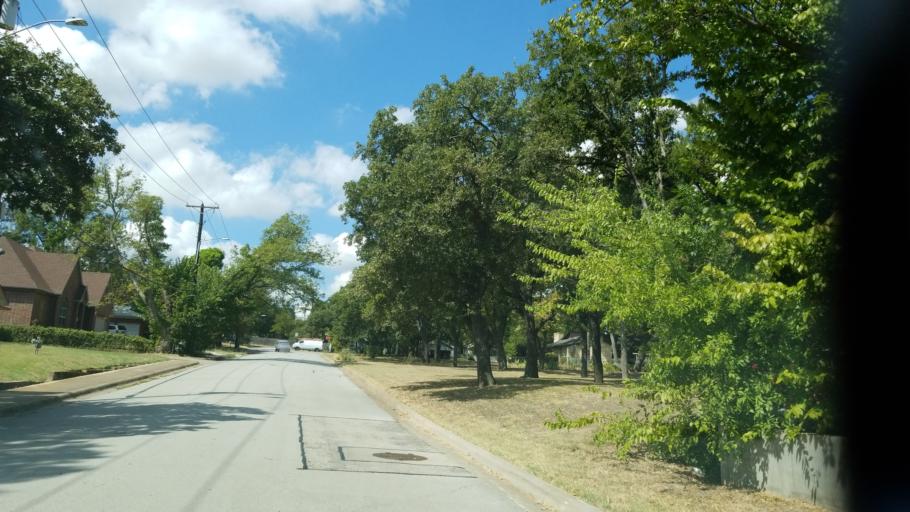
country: US
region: Texas
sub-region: Tarrant County
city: Euless
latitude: 32.8316
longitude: -97.0810
